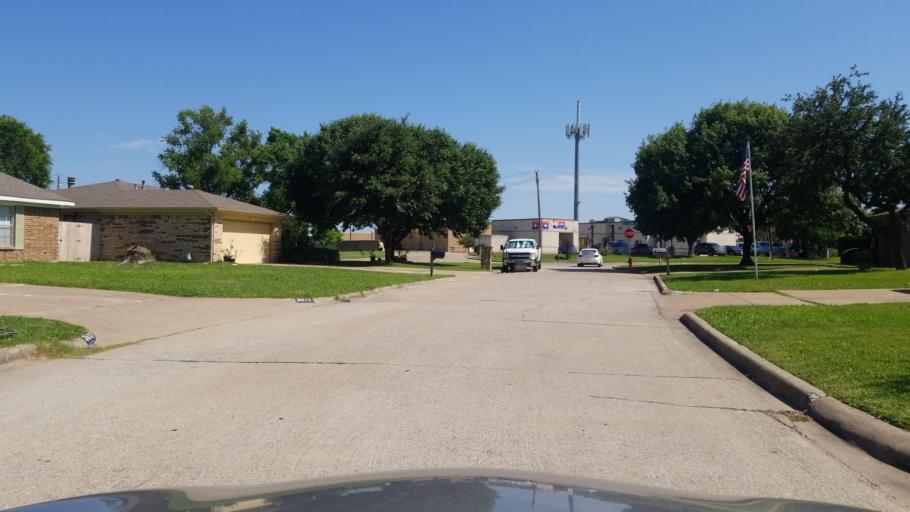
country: US
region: Texas
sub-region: Dallas County
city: Grand Prairie
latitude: 32.6855
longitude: -97.0084
